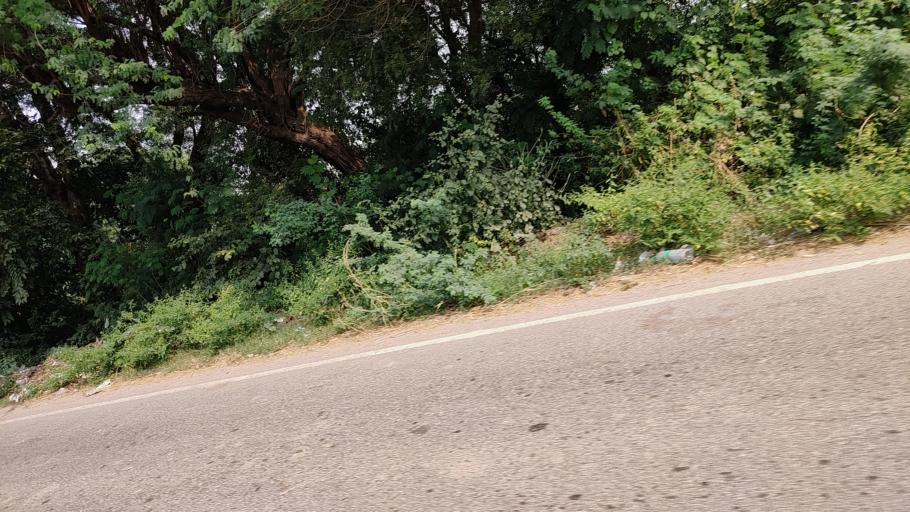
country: IN
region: Uttar Pradesh
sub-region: Mathura
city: Barsana
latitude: 27.6606
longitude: 77.3822
